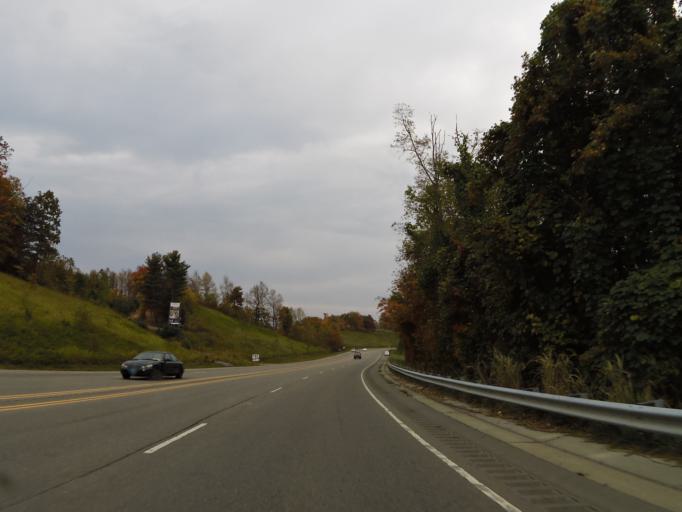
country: US
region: North Carolina
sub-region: Watauga County
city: Blowing Rock
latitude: 36.0849
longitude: -81.6292
